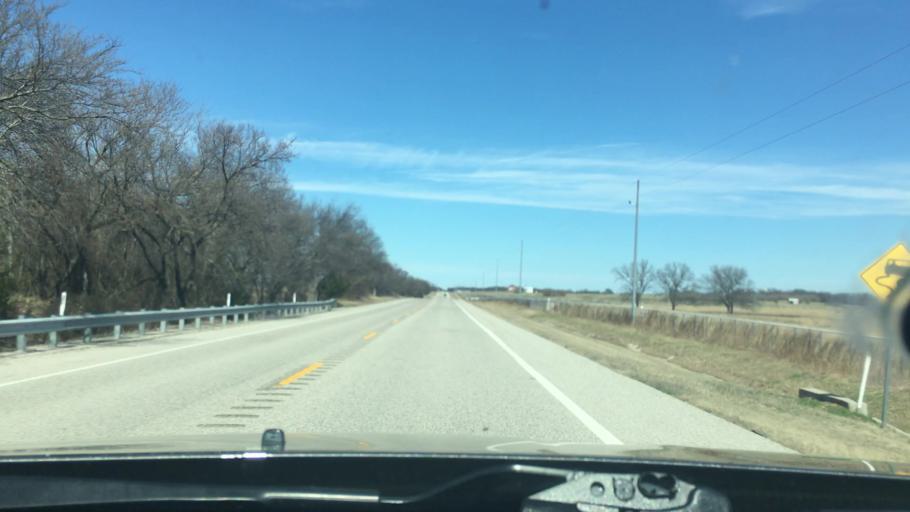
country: US
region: Oklahoma
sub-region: Murray County
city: Sulphur
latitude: 34.3707
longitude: -96.9508
